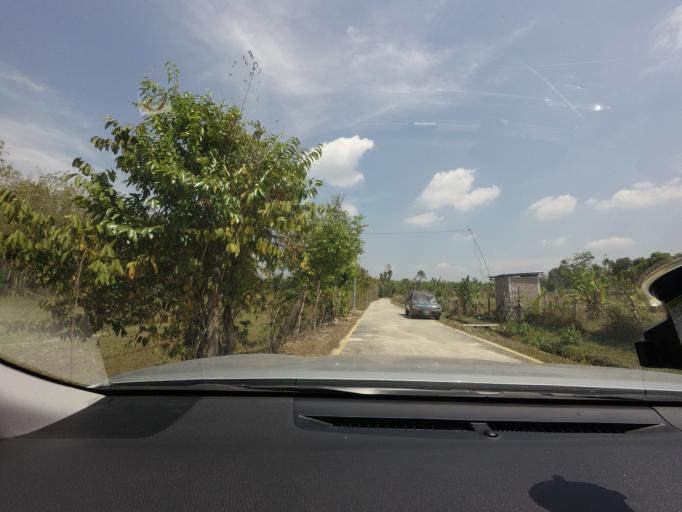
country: TH
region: Narathiwat
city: Rueso
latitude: 6.3821
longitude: 101.4999
